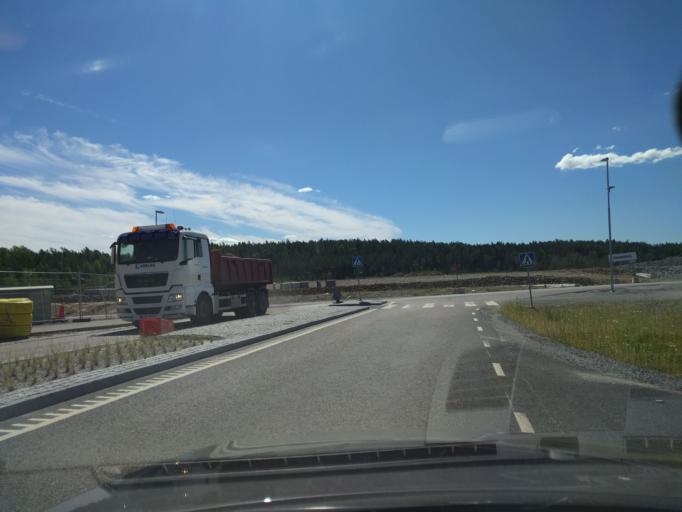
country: SE
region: Stockholm
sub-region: Haninge Kommun
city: Haninge
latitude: 59.1547
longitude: 18.1657
